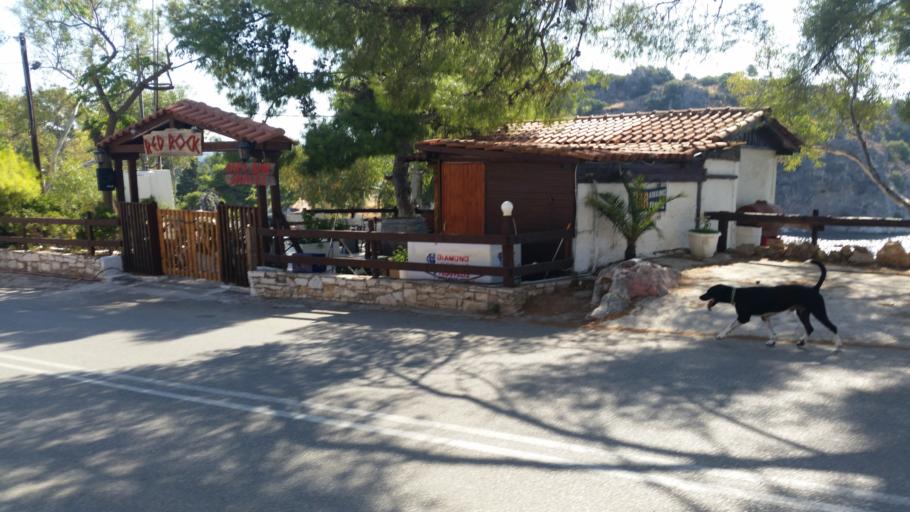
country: GR
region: Peloponnese
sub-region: Nomos Argolidos
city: Tolon
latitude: 37.5282
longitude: 22.8712
